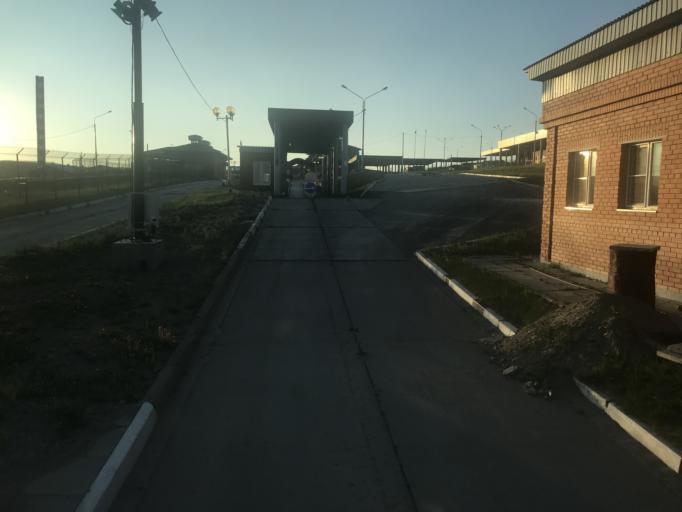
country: MN
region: Selenge
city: Altanbulag
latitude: 50.3239
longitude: 106.4890
